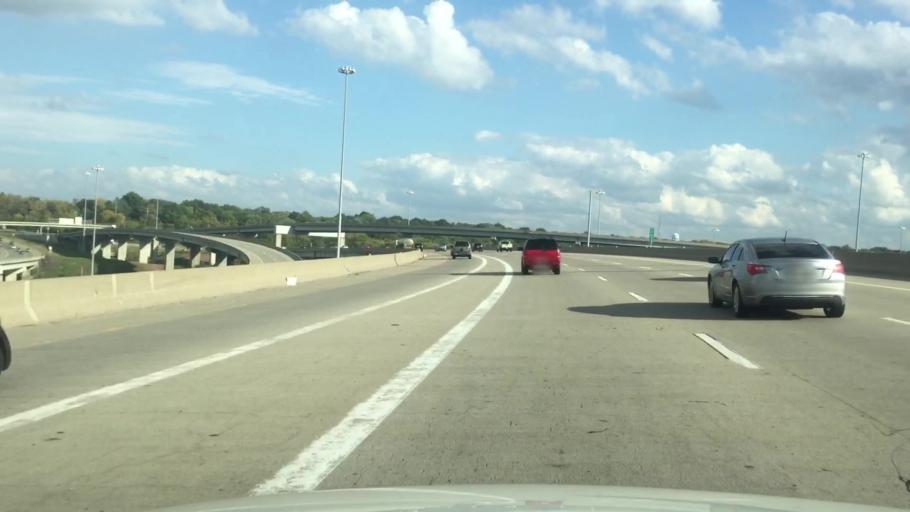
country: US
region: Missouri
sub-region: Jackson County
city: Grandview
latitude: 38.9338
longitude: -94.5307
